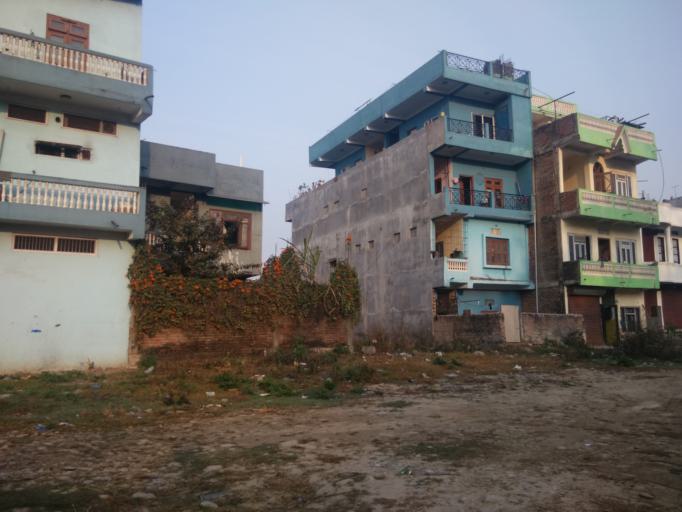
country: NP
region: Central Region
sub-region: Narayani Zone
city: Bharatpur
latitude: 27.6937
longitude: 84.4263
